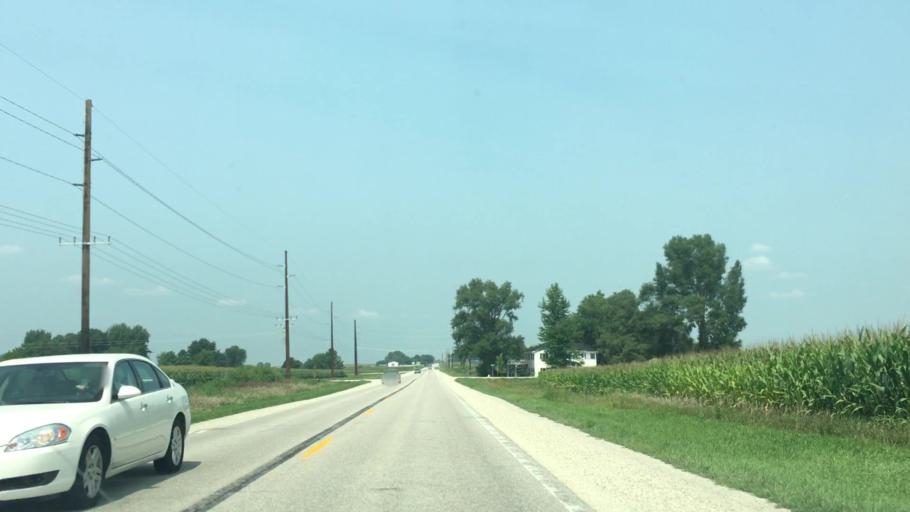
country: US
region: Iowa
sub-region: Buchanan County
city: Independence
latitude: 42.4061
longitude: -91.8899
